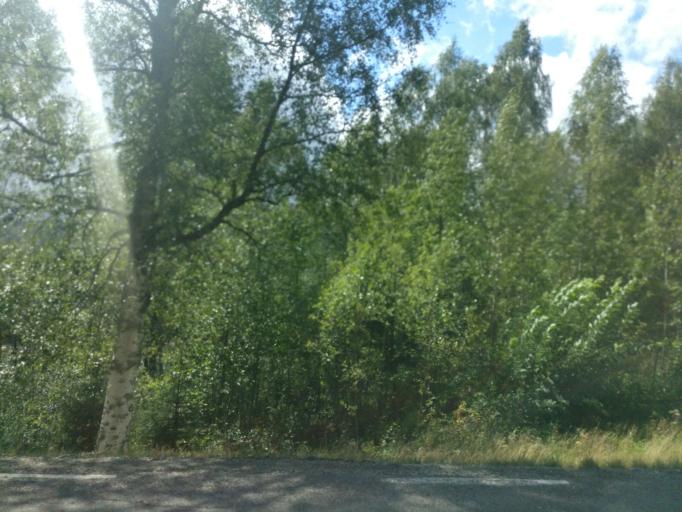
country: SE
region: Vaermland
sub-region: Hagfors Kommun
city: Ekshaerad
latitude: 60.3609
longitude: 13.3161
